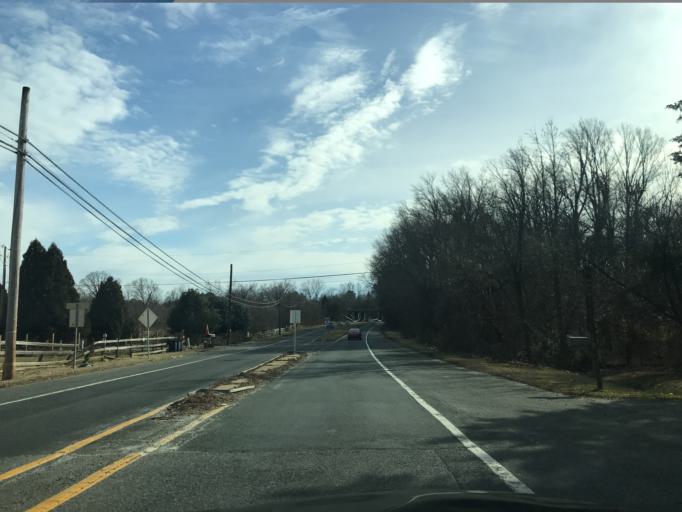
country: US
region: Maryland
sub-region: Prince George's County
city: Woodmore
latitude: 38.9475
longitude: -76.7985
